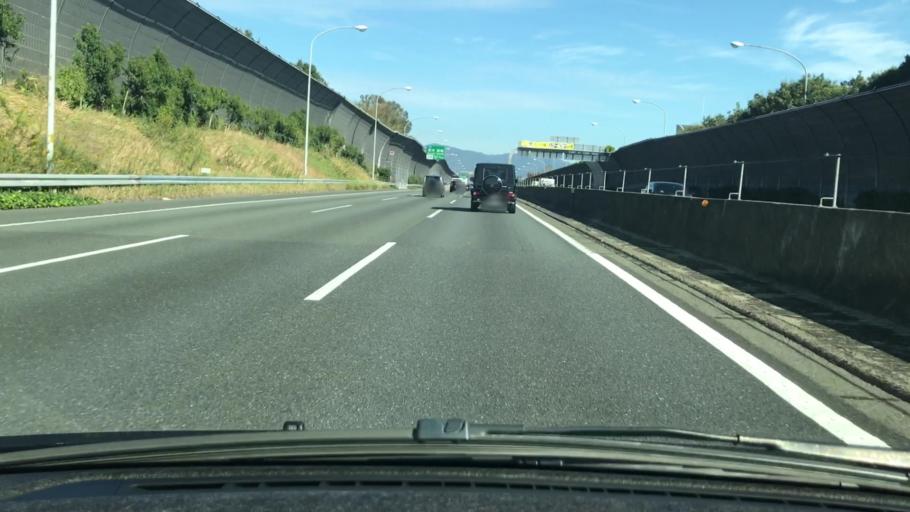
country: JP
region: Osaka
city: Ibaraki
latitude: 34.8207
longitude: 135.5524
